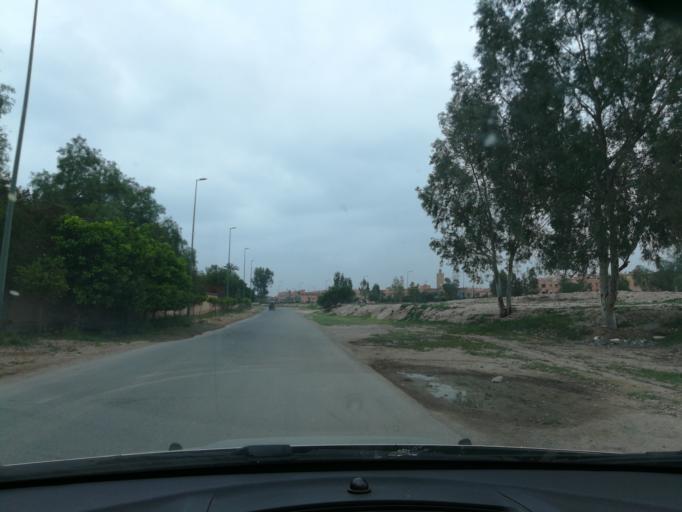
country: MA
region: Marrakech-Tensift-Al Haouz
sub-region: Marrakech
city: Marrakesh
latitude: 31.6561
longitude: -7.9836
